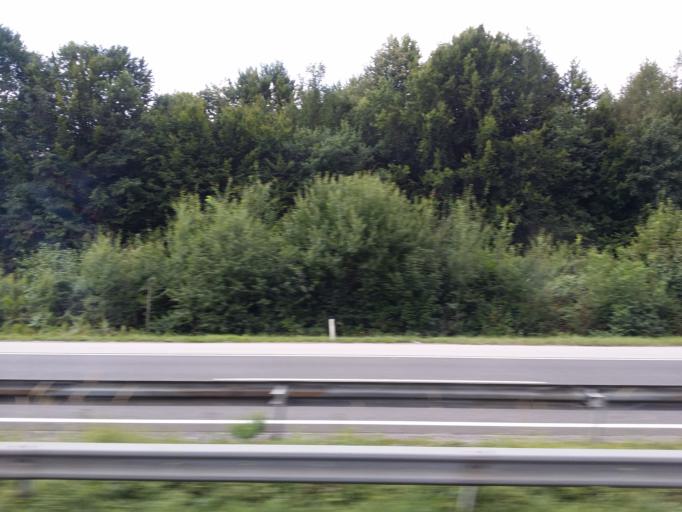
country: SI
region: Kranj
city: Britof
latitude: 46.2577
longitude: 14.3764
